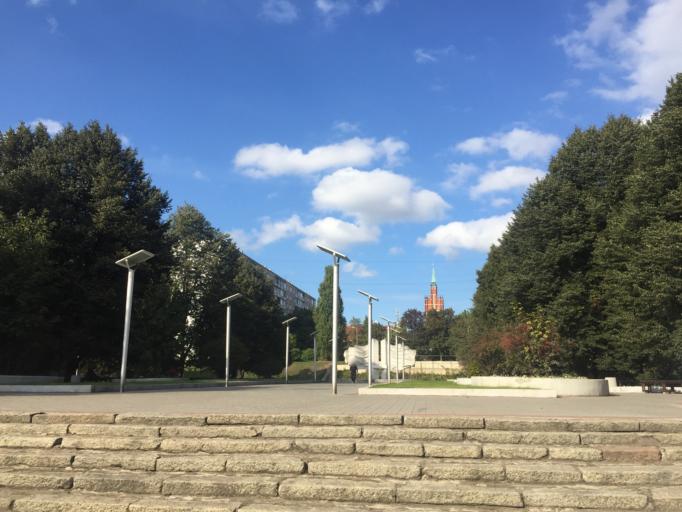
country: RU
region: Kaliningrad
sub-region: Gorod Kaliningrad
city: Kaliningrad
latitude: 54.6951
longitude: 20.5099
